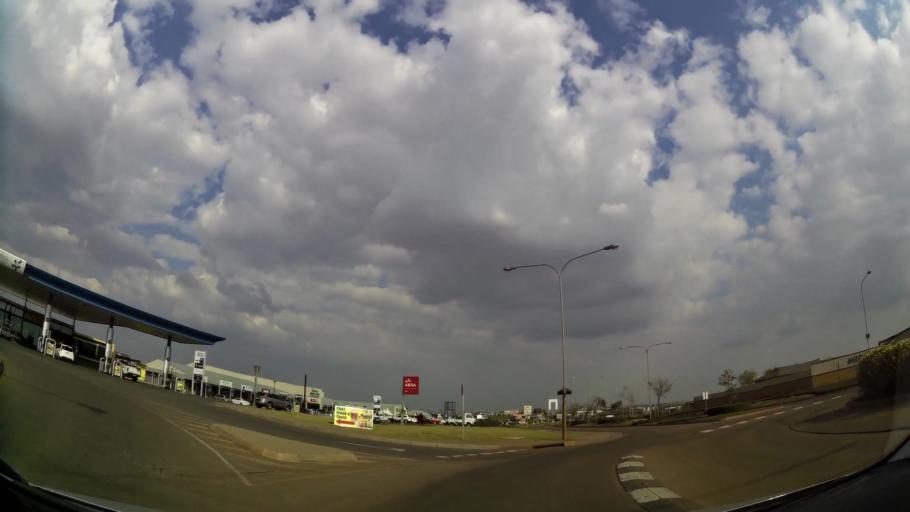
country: ZA
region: Gauteng
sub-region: City of Tshwane Metropolitan Municipality
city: Centurion
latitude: -25.9183
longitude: 28.2103
